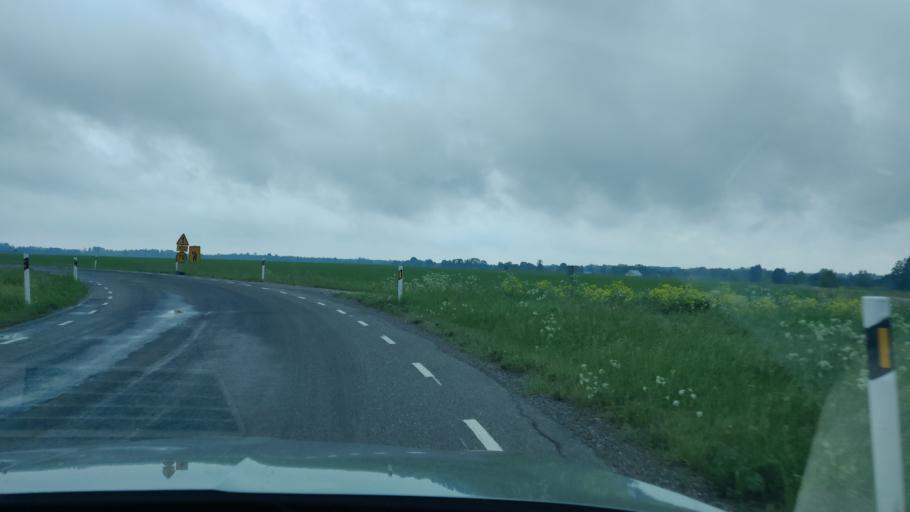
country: EE
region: Jaervamaa
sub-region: Paide linn
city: Paide
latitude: 58.8782
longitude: 25.6738
